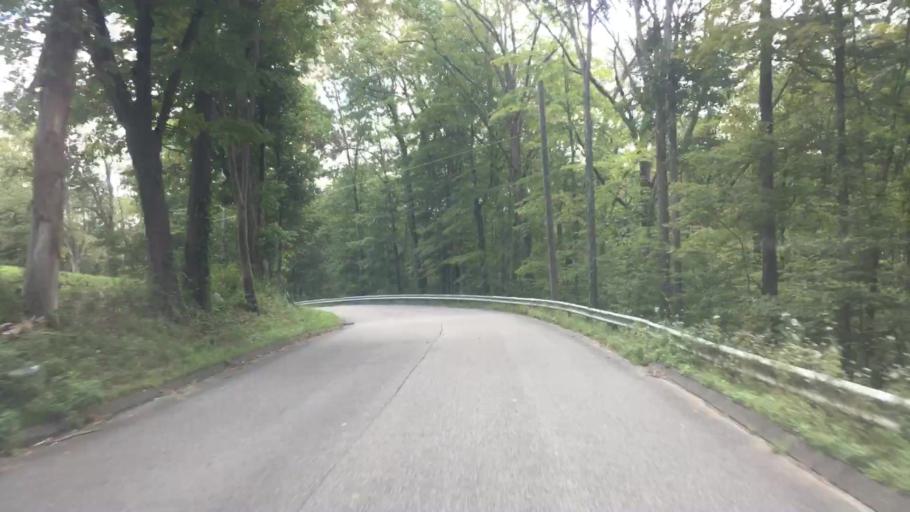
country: US
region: Connecticut
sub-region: Tolland County
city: Stafford Springs
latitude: 41.9180
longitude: -72.2247
